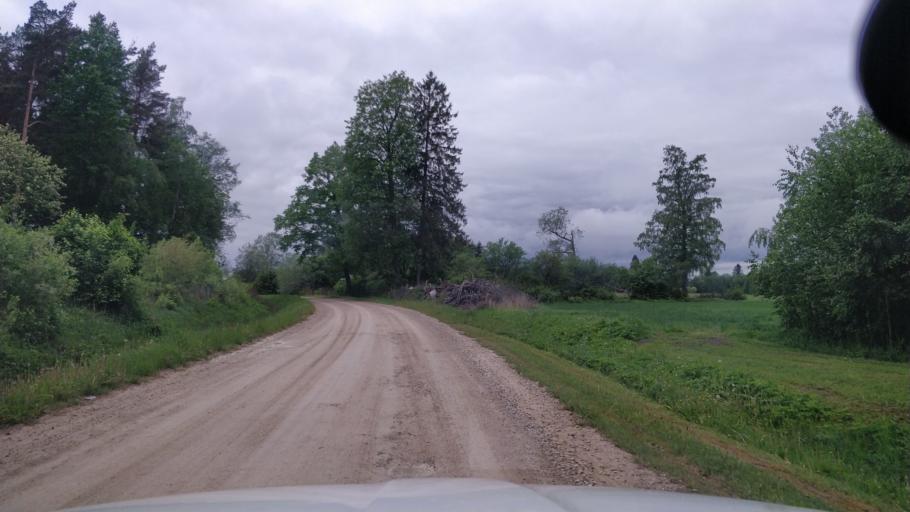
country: EE
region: Paernumaa
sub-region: Halinga vald
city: Parnu-Jaagupi
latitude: 58.7100
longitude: 24.3484
